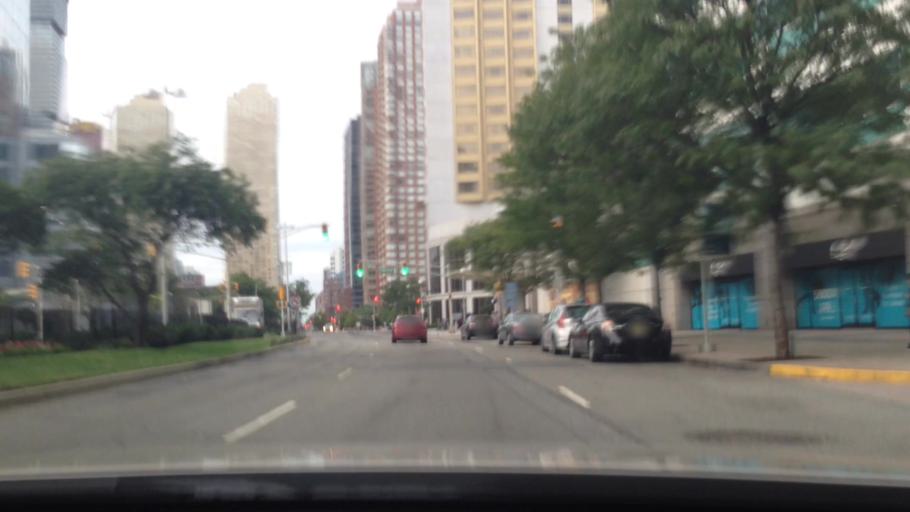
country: US
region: New Jersey
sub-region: Hudson County
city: Hoboken
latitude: 40.7258
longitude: -74.0354
